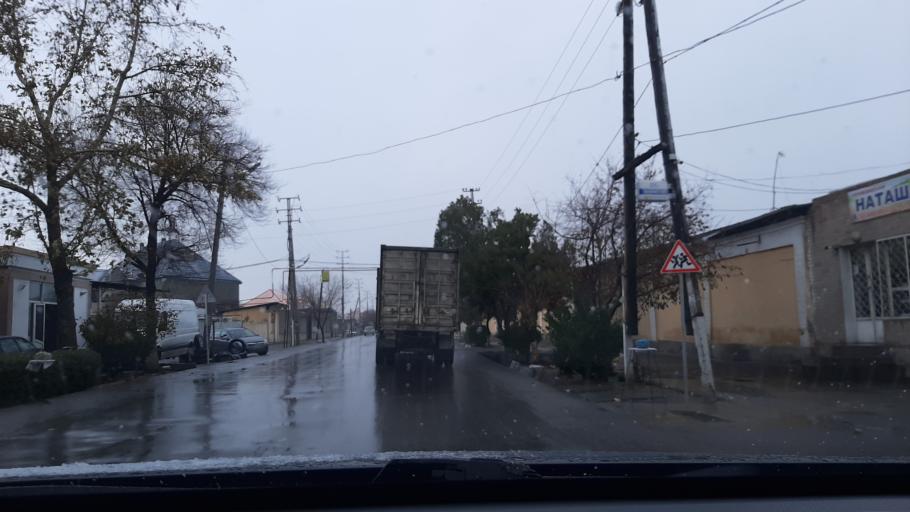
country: TJ
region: Viloyati Sughd
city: Khujand
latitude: 40.2698
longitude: 69.6306
